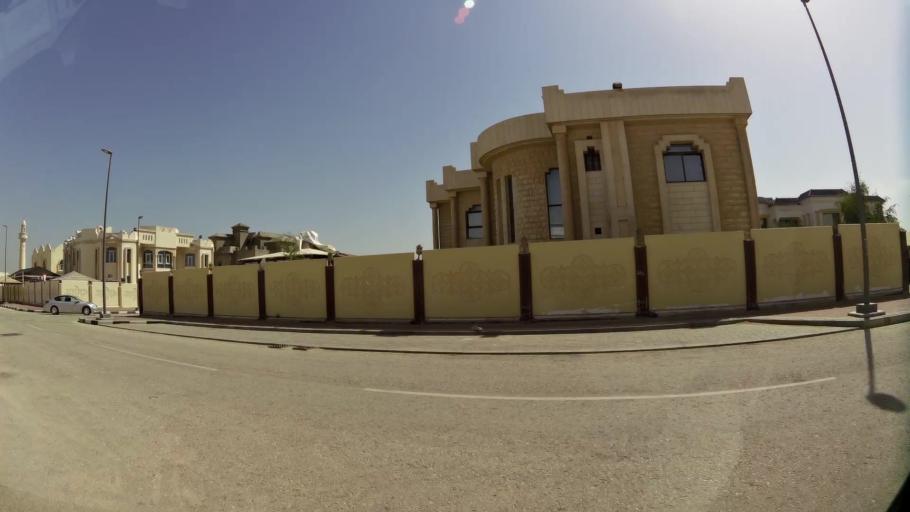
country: QA
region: Baladiyat ad Dawhah
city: Doha
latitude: 25.3556
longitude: 51.4967
